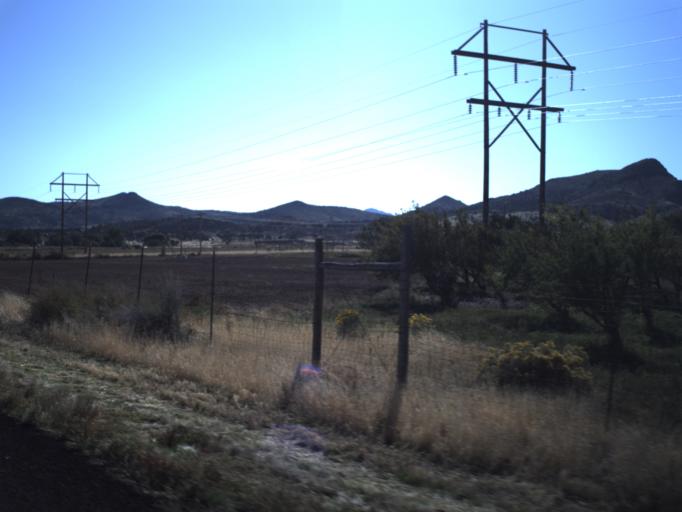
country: US
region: Utah
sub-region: Washington County
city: Enterprise
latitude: 37.6722
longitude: -113.5468
